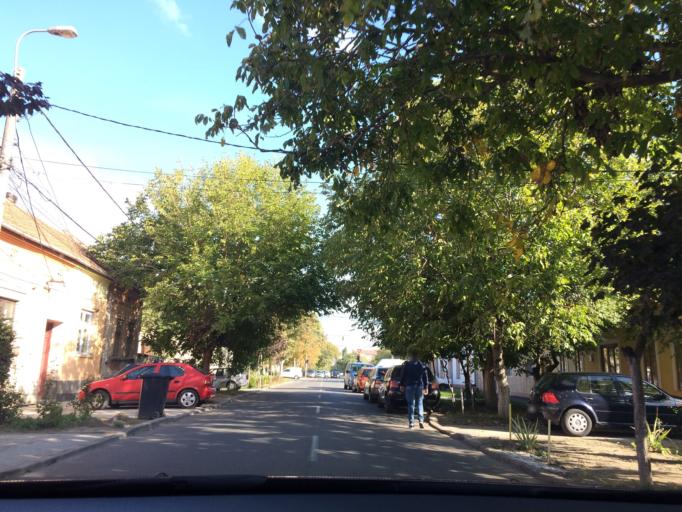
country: RO
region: Timis
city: Timisoara
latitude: 45.7637
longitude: 21.2048
